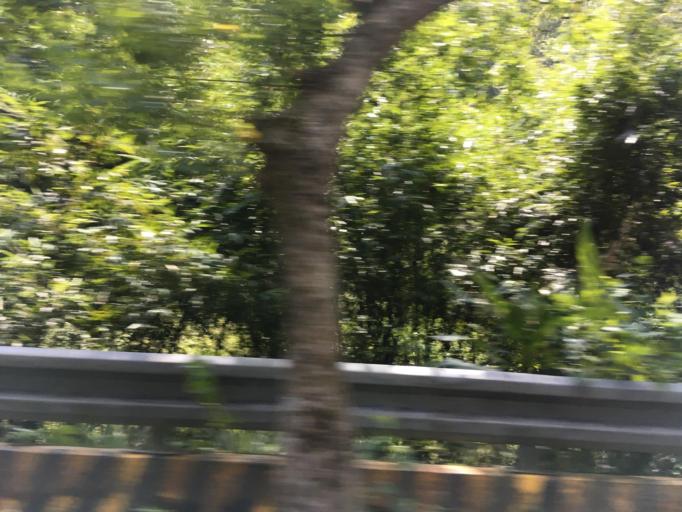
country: TW
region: Taiwan
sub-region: Yilan
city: Yilan
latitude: 24.8165
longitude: 121.7370
